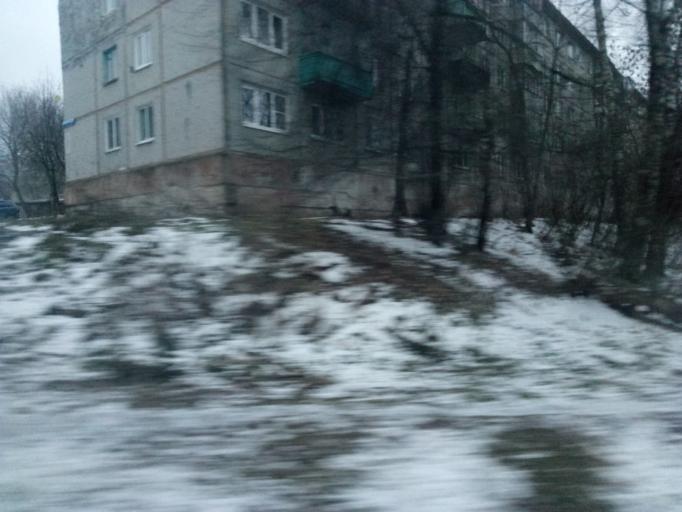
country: RU
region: Tula
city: Kosaya Gora
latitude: 54.1984
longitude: 37.5327
